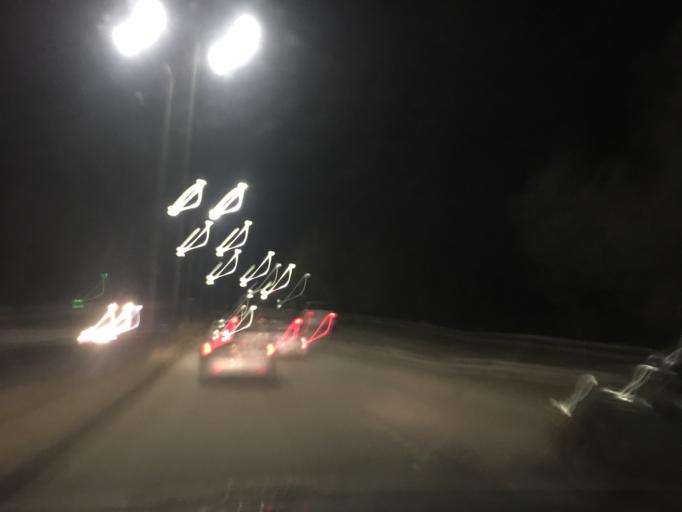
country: JO
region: Amman
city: Umm as Summaq
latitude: 31.8830
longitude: 35.8428
